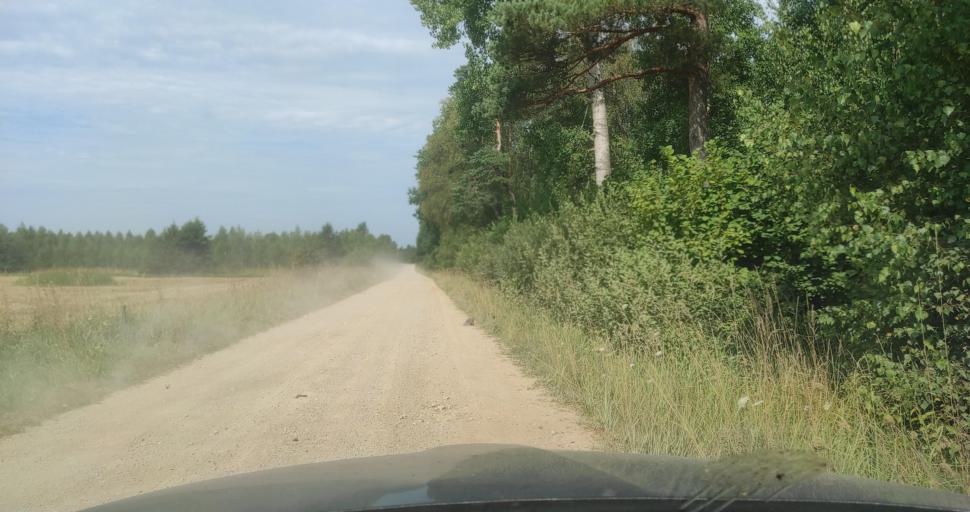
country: LV
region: Kuldigas Rajons
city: Kuldiga
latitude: 56.9829
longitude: 22.0703
